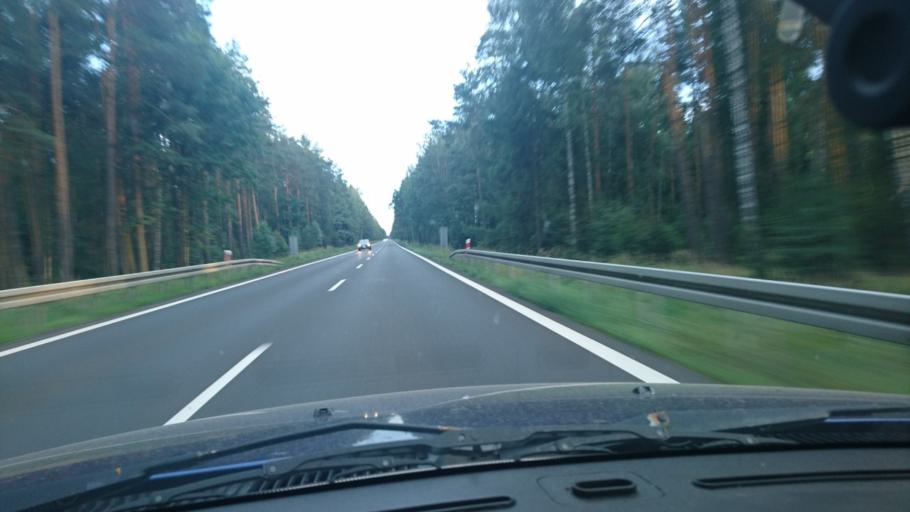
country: PL
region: Silesian Voivodeship
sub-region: Powiat tarnogorski
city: Tworog
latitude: 50.5704
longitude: 18.7109
